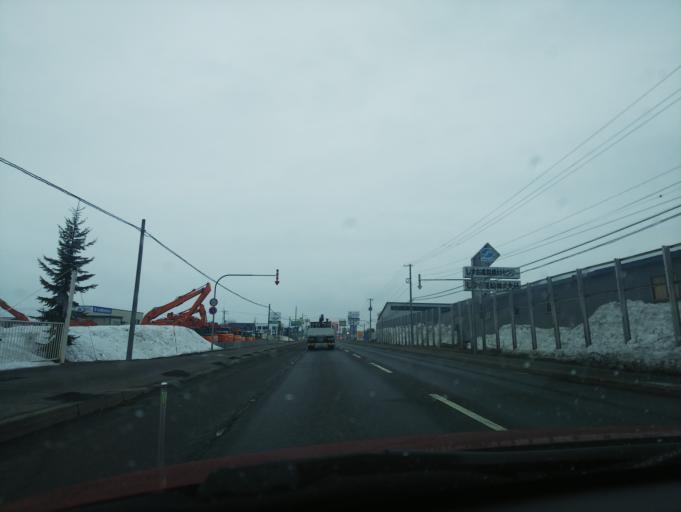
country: JP
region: Hokkaido
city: Nayoro
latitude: 44.1585
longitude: 142.3976
